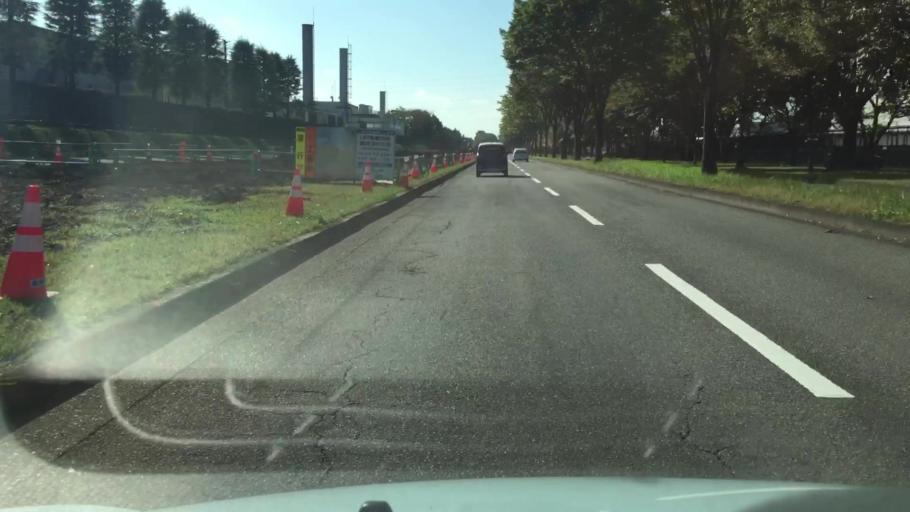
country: JP
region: Tochigi
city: Utsunomiya-shi
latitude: 36.5535
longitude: 139.9831
